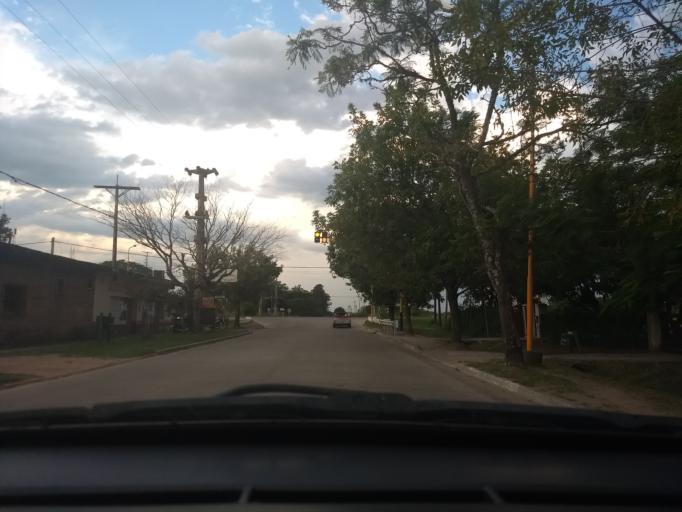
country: AR
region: Corrientes
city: Riachuelo
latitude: -27.5825
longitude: -58.7412
